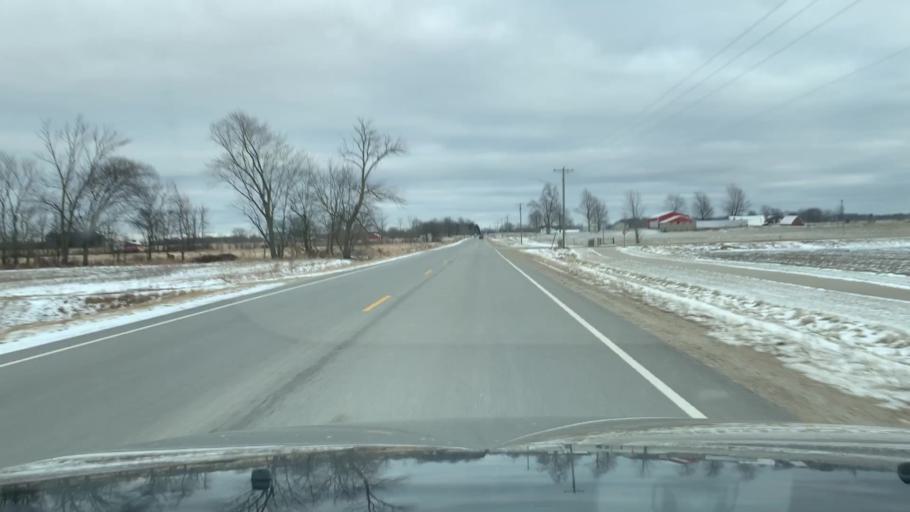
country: US
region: Michigan
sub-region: Ottawa County
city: Hudsonville
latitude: 42.8115
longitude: -85.9117
